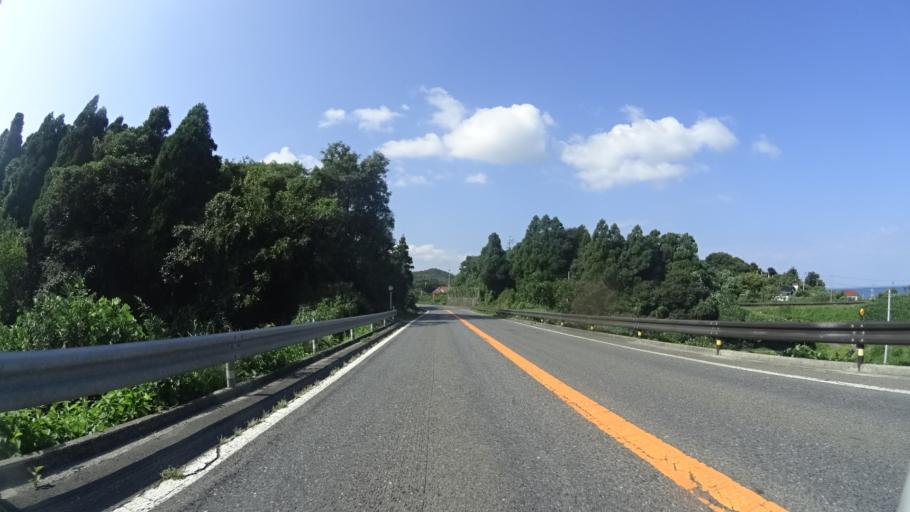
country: JP
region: Shimane
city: Gotsucho
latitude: 35.0570
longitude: 132.3148
